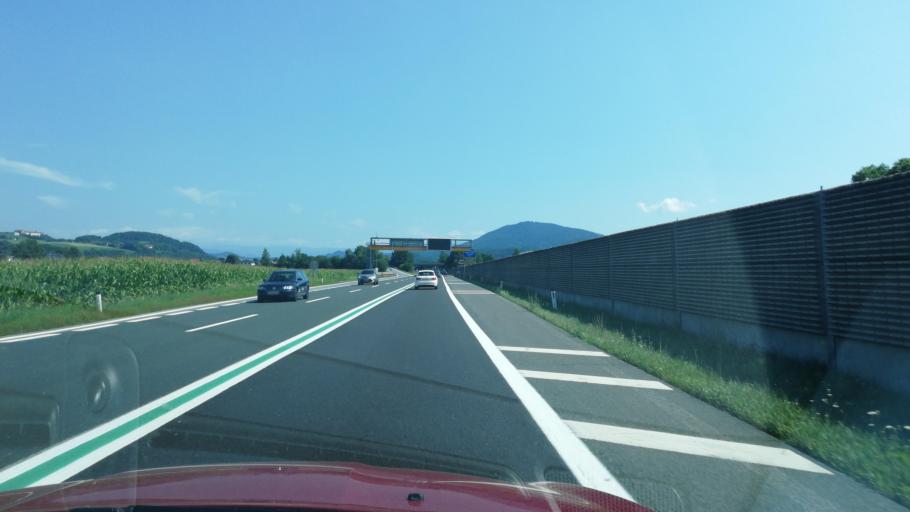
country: AT
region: Carinthia
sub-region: Politischer Bezirk Klagenfurt Land
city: Maria Saal
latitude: 46.6793
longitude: 14.3319
